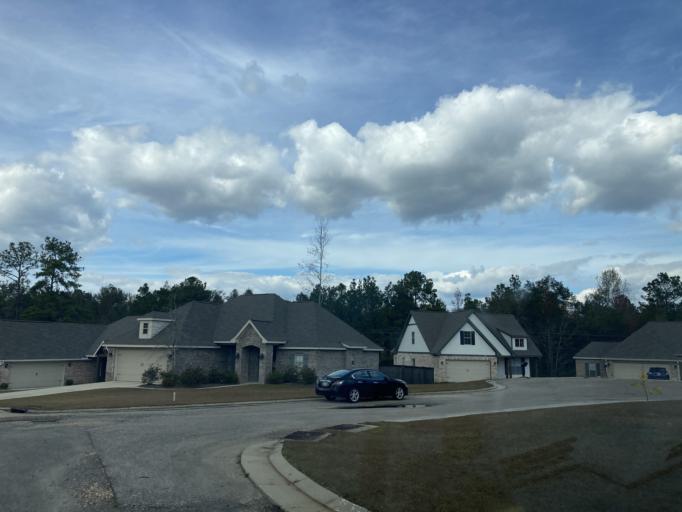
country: US
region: Mississippi
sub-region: Lamar County
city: Arnold Line
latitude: 31.3458
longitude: -89.3901
